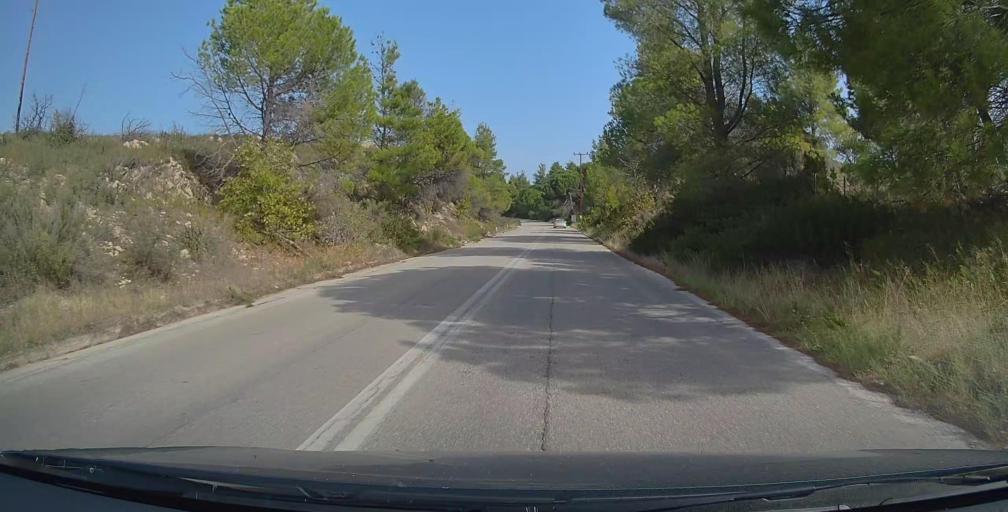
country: GR
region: Central Macedonia
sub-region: Nomos Chalkidikis
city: Sarti
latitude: 40.1185
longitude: 23.9707
